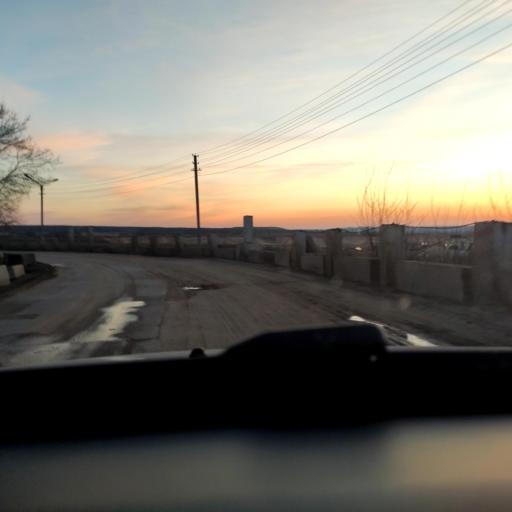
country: RU
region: Voronezj
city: Podgornoye
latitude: 51.7093
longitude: 39.1326
